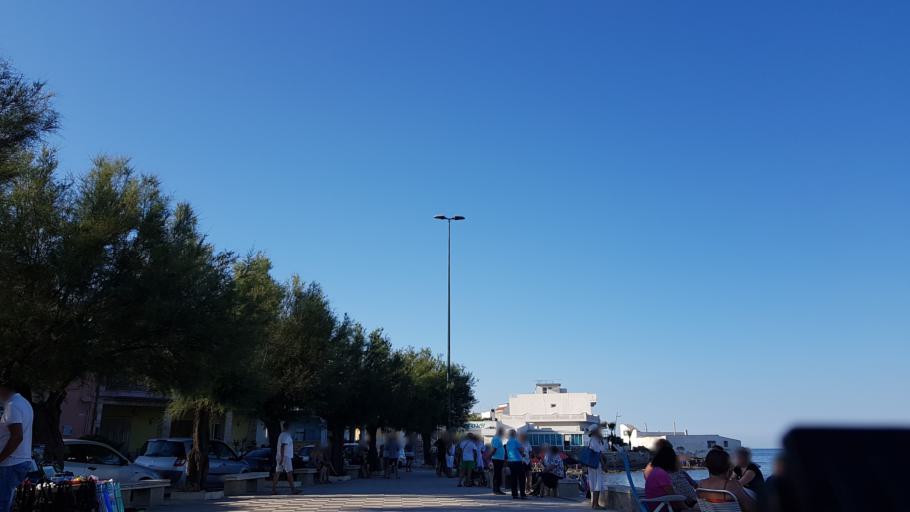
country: IT
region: Apulia
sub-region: Provincia di Brindisi
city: Torchiarolo
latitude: 40.5351
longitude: 18.0752
